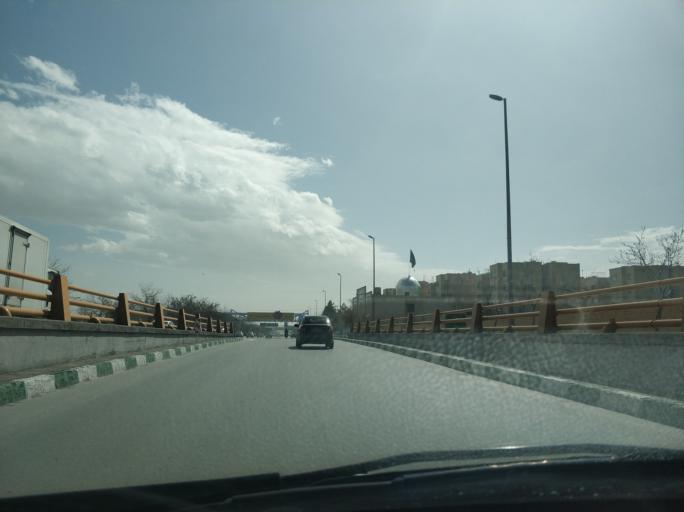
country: IR
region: Razavi Khorasan
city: Torqabeh
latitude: 36.3416
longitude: 59.4551
